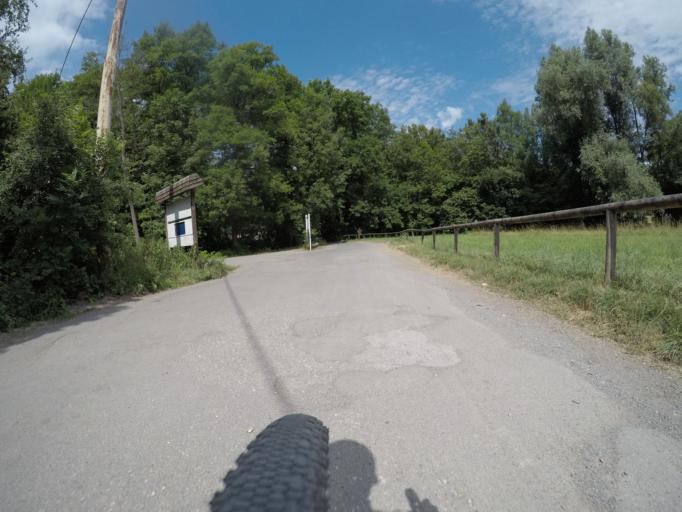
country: DE
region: Baden-Wuerttemberg
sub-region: Regierungsbezirk Stuttgart
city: Stuttgart Feuerbach
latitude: 48.7875
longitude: 9.1376
